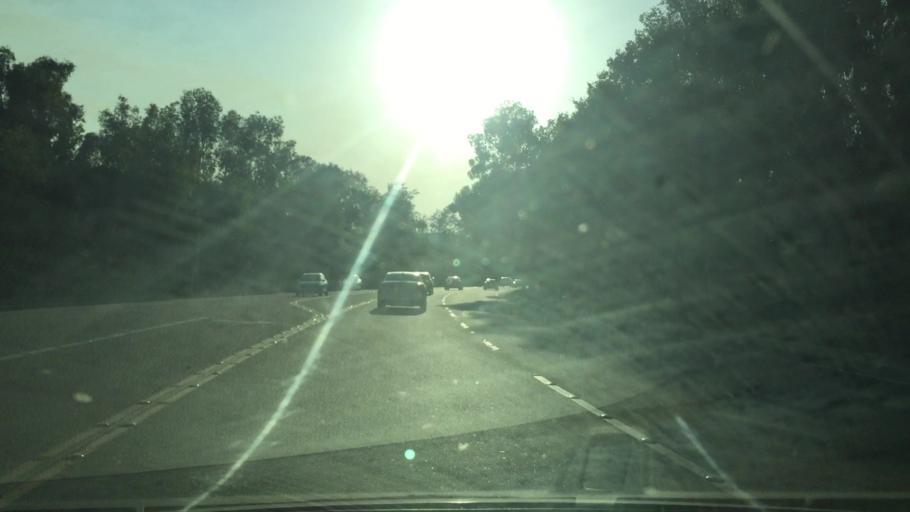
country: US
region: California
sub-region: San Bernardino County
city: Los Serranos
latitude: 33.9301
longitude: -117.6636
